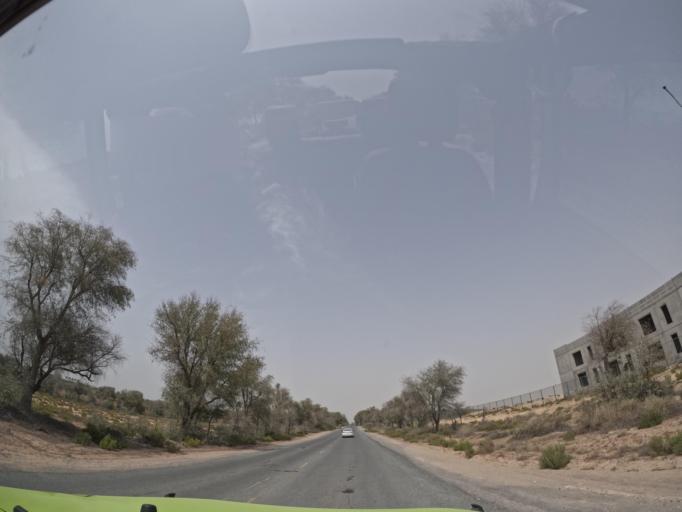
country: AE
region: Dubai
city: Dubai
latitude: 25.1334
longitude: 55.3352
